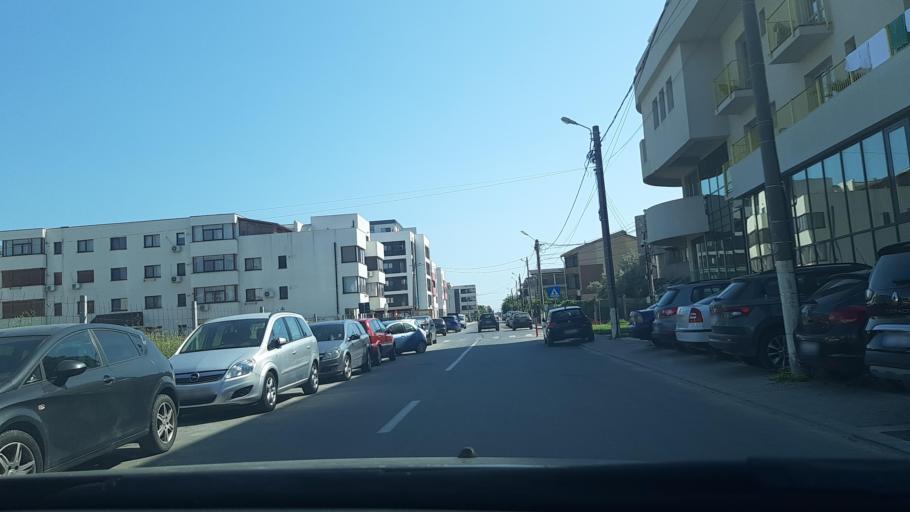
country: RO
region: Constanta
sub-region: Comuna Navodari
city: Navodari
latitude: 44.3056
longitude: 28.6249
